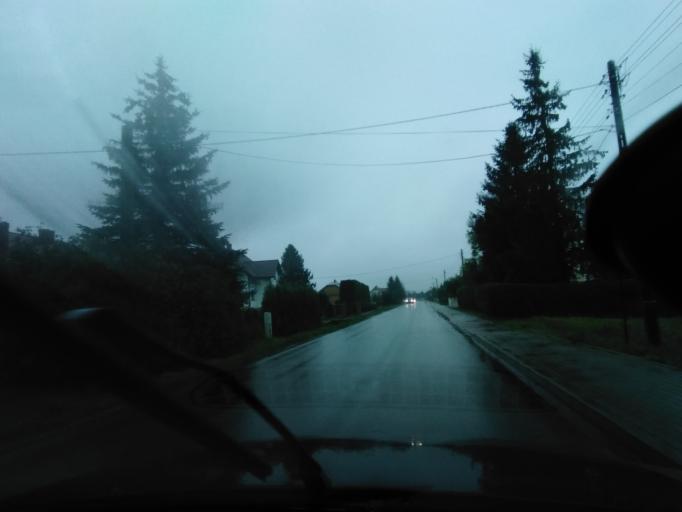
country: PL
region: Subcarpathian Voivodeship
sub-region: Powiat krosnienski
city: Miejsce Piastowe
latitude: 49.6593
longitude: 21.8029
